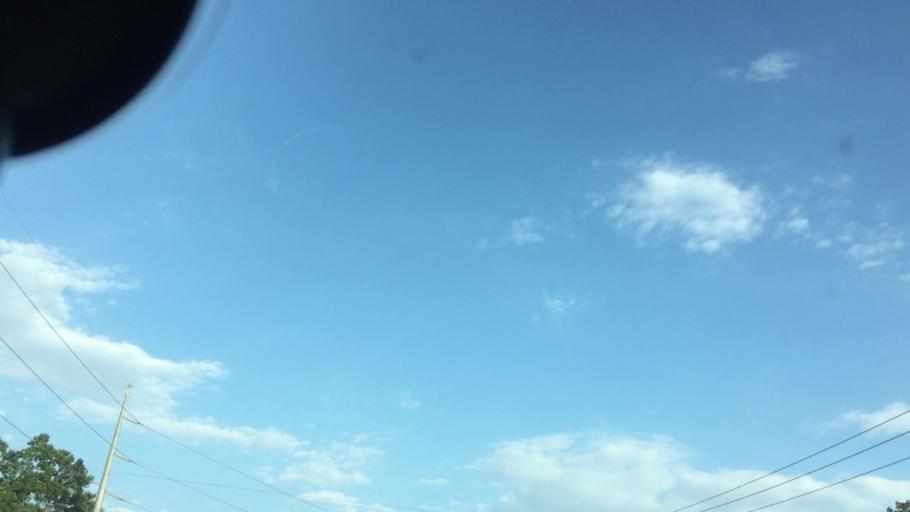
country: US
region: Georgia
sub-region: DeKalb County
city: Panthersville
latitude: 33.6996
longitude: -84.2077
